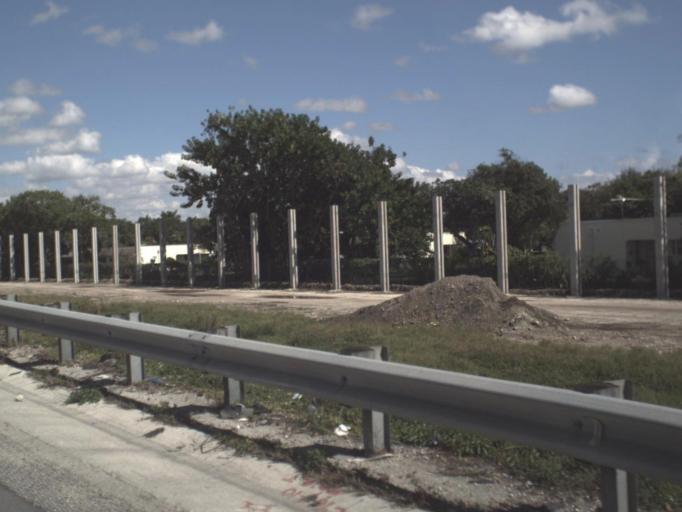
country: US
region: Florida
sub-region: Miami-Dade County
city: South Miami Heights
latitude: 25.6102
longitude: -80.3781
